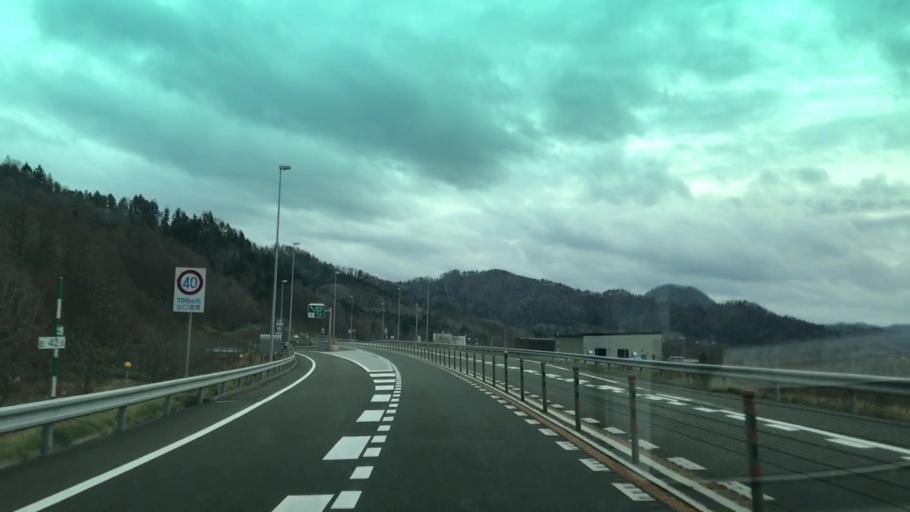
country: JP
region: Hokkaido
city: Iwamizawa
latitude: 42.9264
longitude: 142.0362
